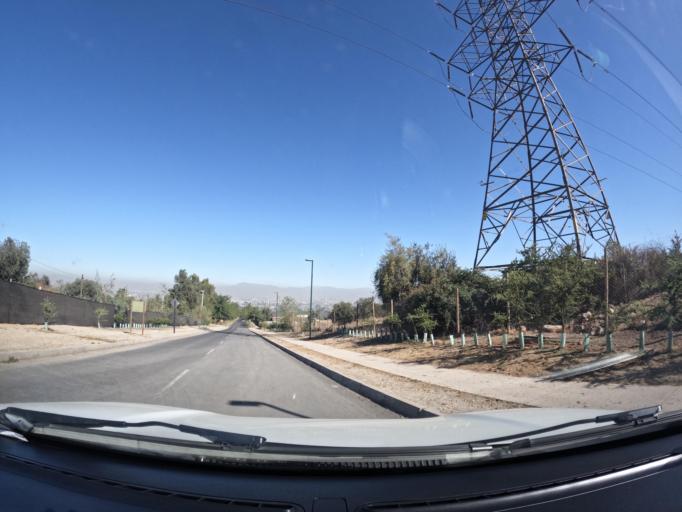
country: CL
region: Santiago Metropolitan
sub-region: Provincia de Santiago
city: Villa Presidente Frei, Nunoa, Santiago, Chile
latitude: -33.5016
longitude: -70.5189
